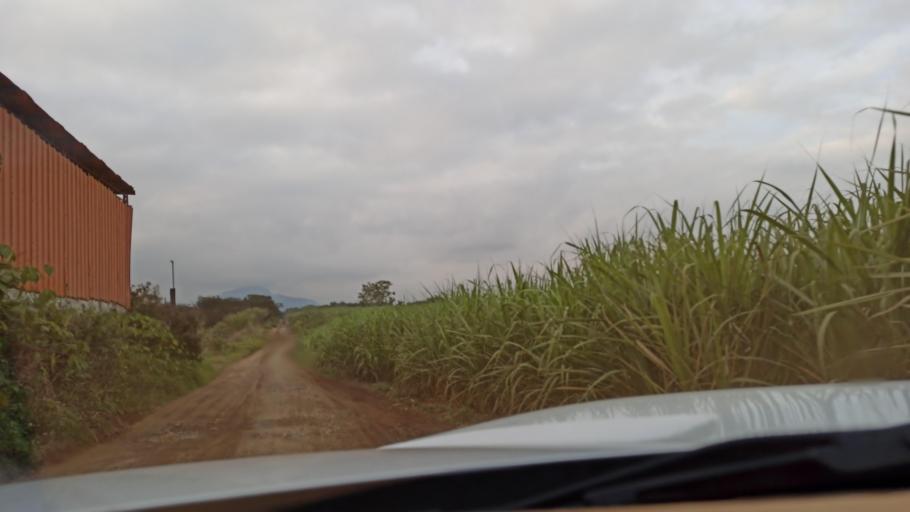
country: MX
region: Veracruz
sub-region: Fortin
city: Monte Salas
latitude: 18.9254
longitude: -97.0061
